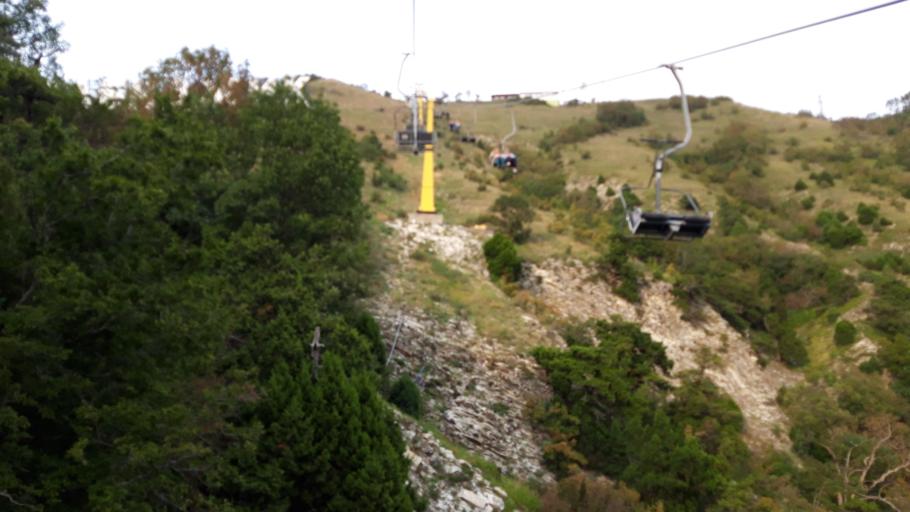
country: RU
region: Krasnodarskiy
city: Gelendzhik
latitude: 44.5825
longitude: 38.0985
